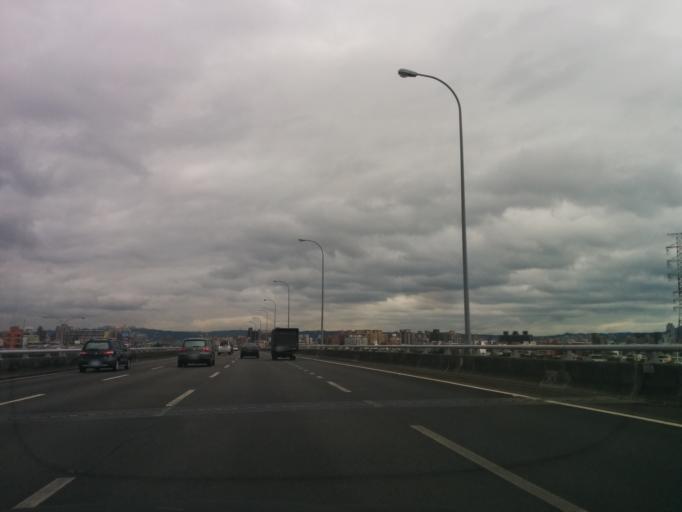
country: TW
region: Taipei
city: Taipei
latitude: 25.0783
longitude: 121.5049
